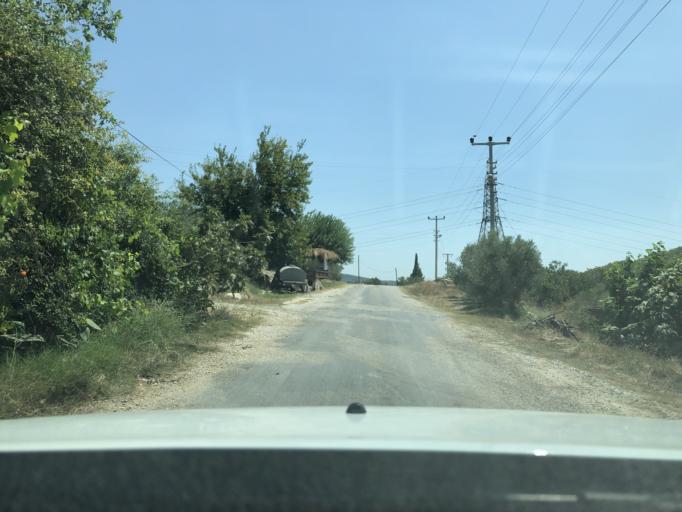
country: TR
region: Antalya
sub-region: Manavgat
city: Kizilagac
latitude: 36.8578
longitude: 31.5562
